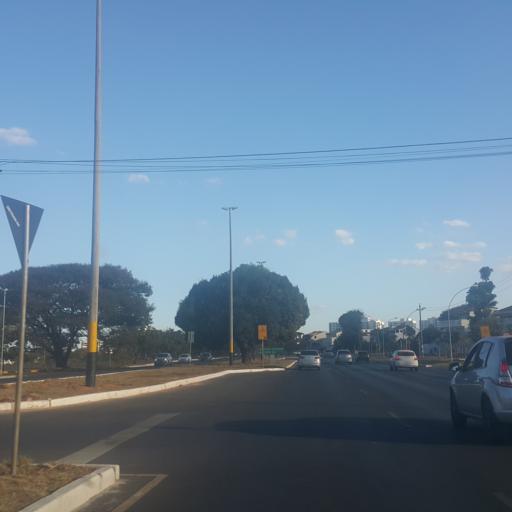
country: BR
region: Federal District
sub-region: Brasilia
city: Brasilia
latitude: -15.8316
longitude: -47.9746
